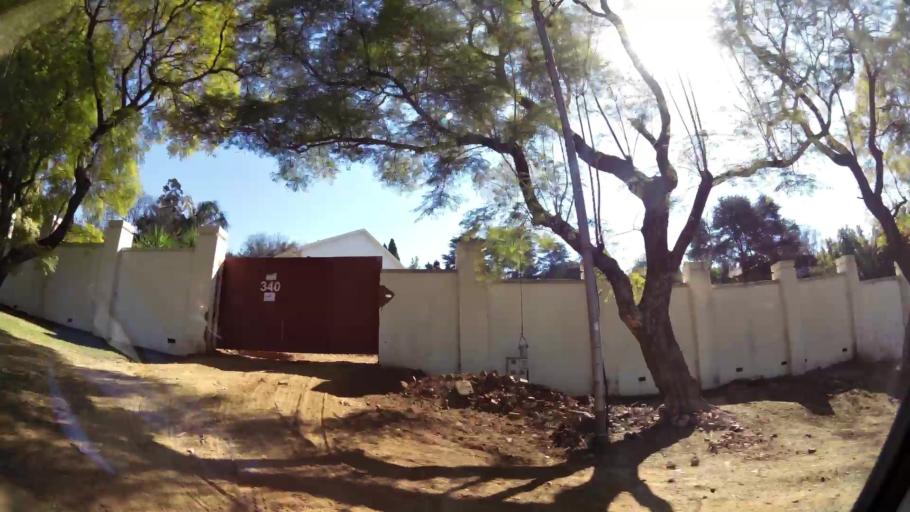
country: ZA
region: Gauteng
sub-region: City of Tshwane Metropolitan Municipality
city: Pretoria
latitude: -25.7888
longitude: 28.2426
